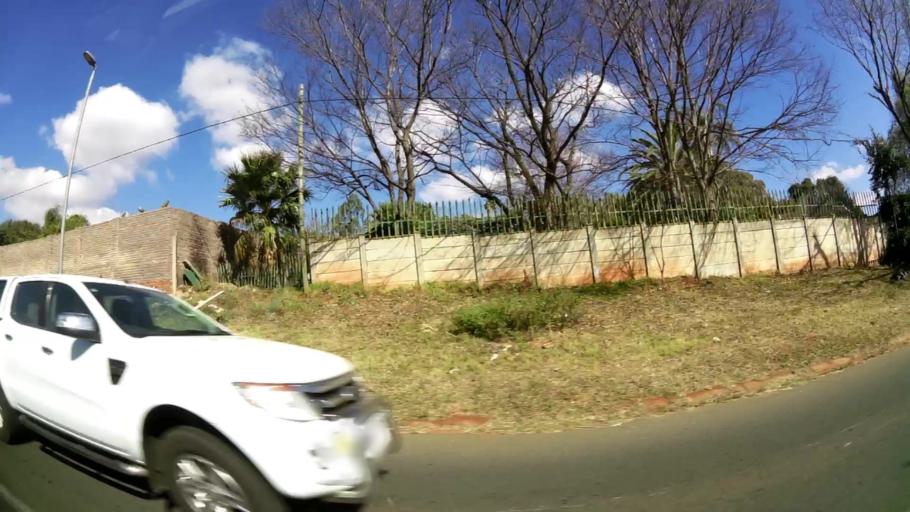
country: ZA
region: Gauteng
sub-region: City of Johannesburg Metropolitan Municipality
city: Roodepoort
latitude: -26.1113
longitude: 27.8389
